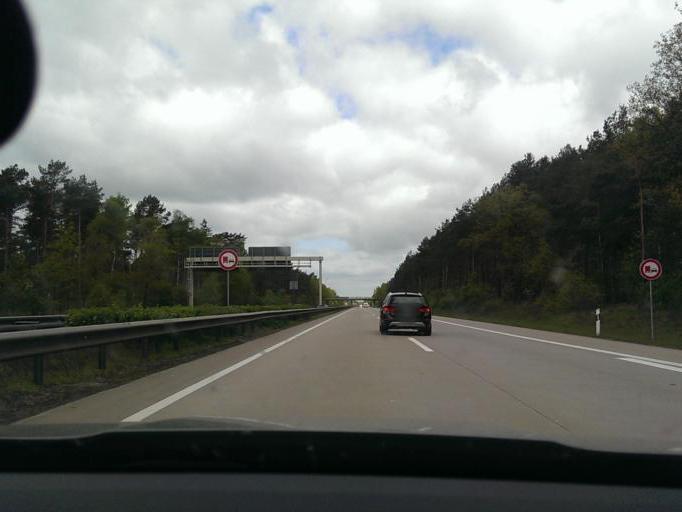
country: DE
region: Lower Saxony
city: Bad Fallingbostel
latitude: 52.7910
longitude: 9.6624
